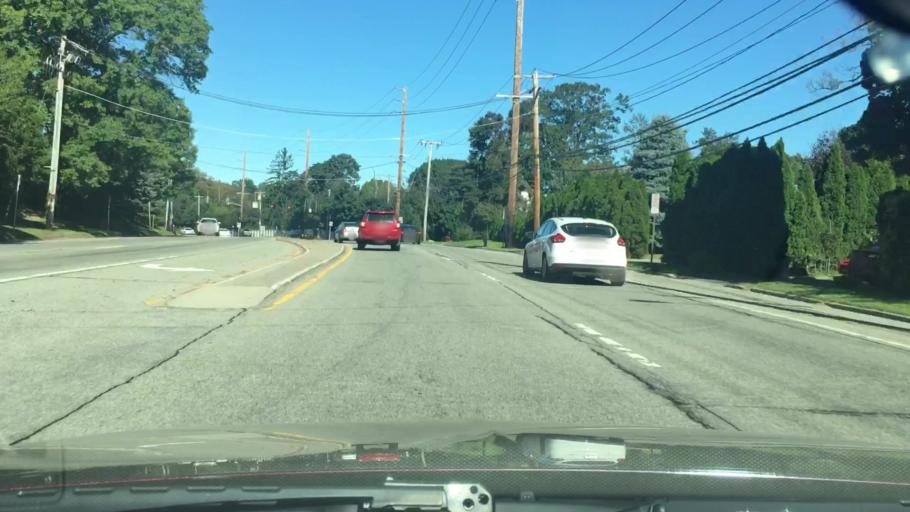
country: US
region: New York
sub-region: Nassau County
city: Roslyn Estates
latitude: 40.8035
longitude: -73.6685
